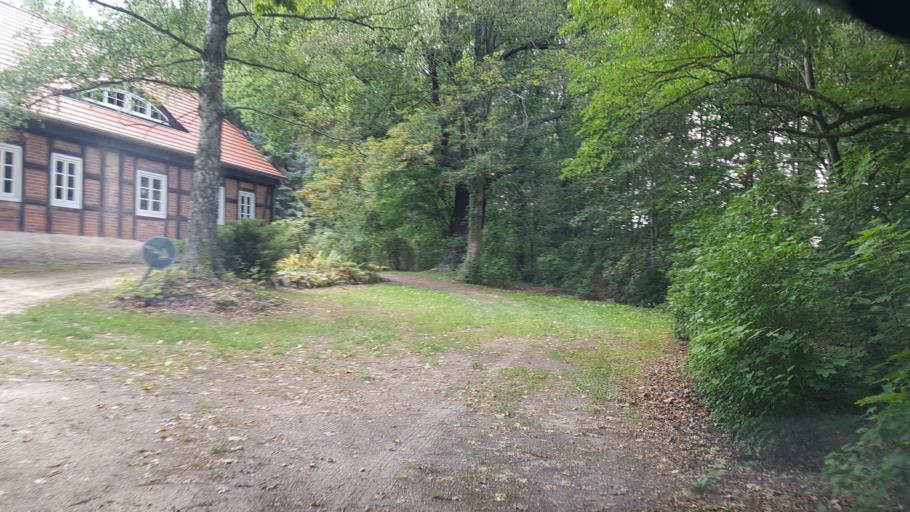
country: DE
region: Brandenburg
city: Calau
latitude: 51.7161
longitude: 13.9434
